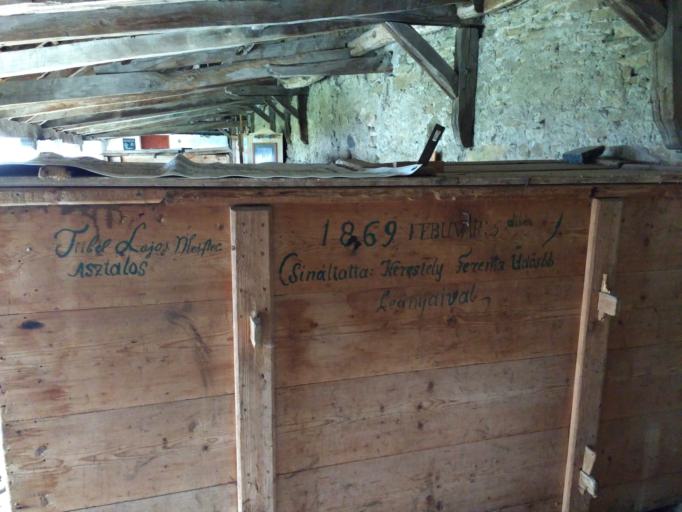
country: RO
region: Harghita
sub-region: Comuna Darjiu
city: Darjiu
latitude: 46.2023
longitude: 25.1992
